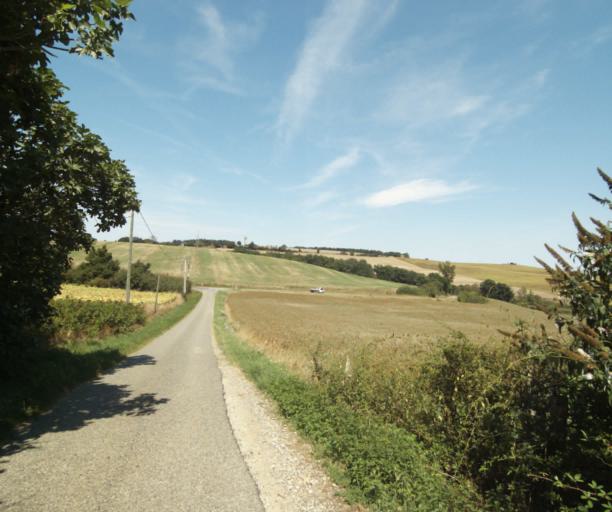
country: FR
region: Midi-Pyrenees
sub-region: Departement de l'Ariege
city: Lezat-sur-Leze
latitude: 43.2706
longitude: 1.3096
